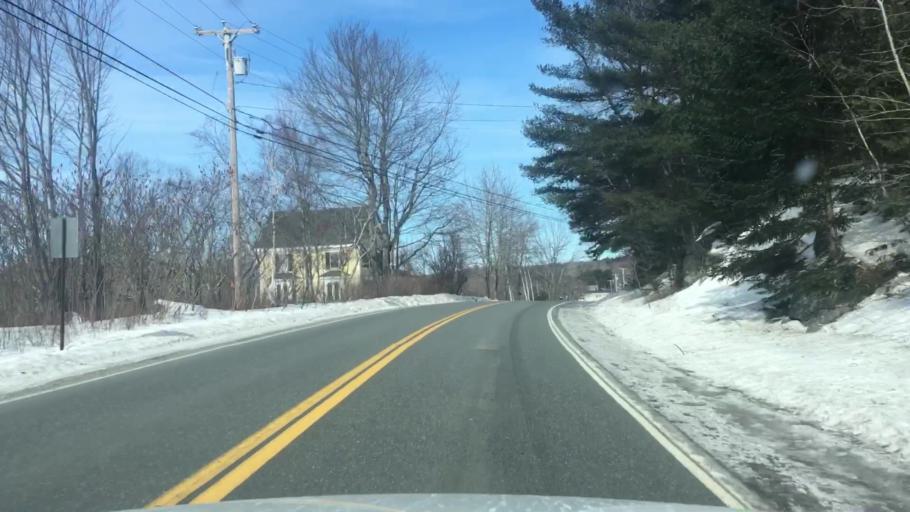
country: US
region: Maine
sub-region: Hancock County
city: Orland
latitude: 44.5473
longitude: -68.7429
